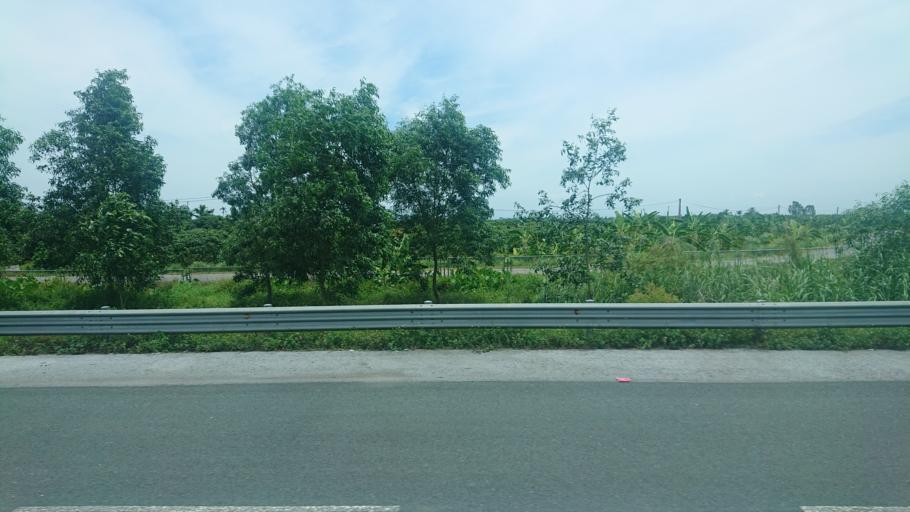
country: VN
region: Hai Phong
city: An Lao
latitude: 20.8154
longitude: 106.4926
